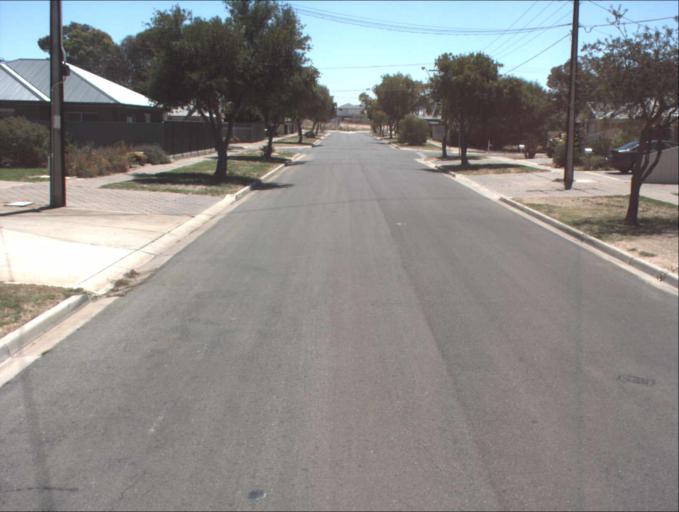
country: AU
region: South Australia
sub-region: Port Adelaide Enfield
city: Klemzig
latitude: -34.8671
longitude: 138.6304
